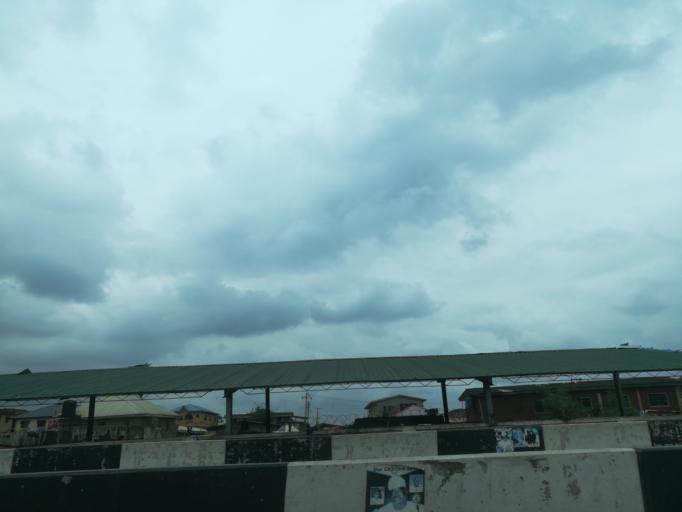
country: NG
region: Lagos
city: Ojota
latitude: 6.6154
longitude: 3.3973
